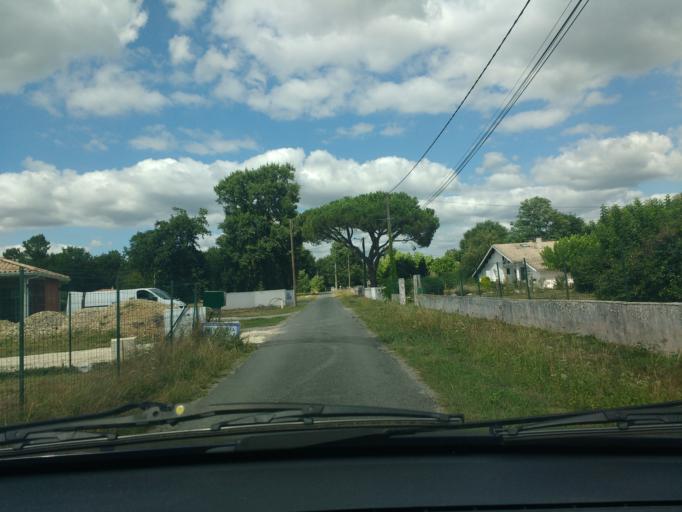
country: FR
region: Aquitaine
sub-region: Departement de la Gironde
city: Salles
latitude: 44.5635
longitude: -0.8419
